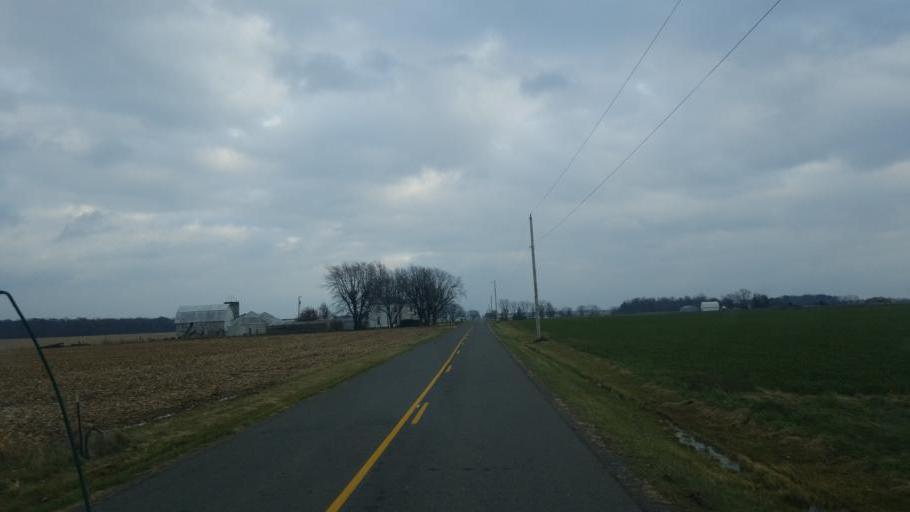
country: US
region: Ohio
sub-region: Mercer County
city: Coldwater
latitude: 40.5090
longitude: -84.6986
